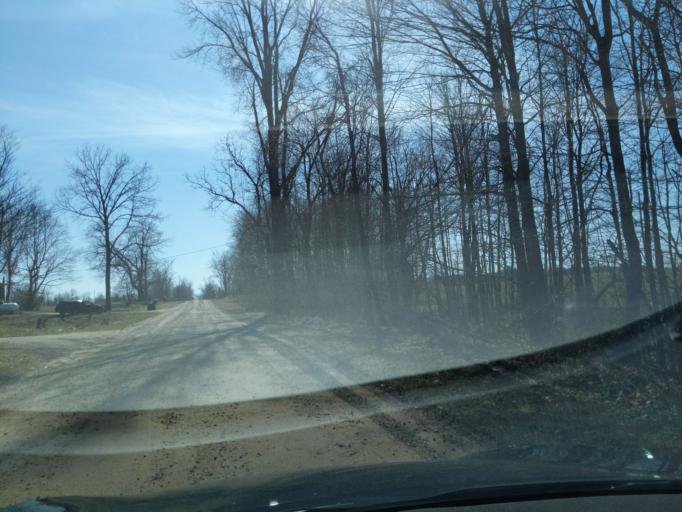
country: US
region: Michigan
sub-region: Ionia County
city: Lake Odessa
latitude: 42.7245
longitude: -85.0539
